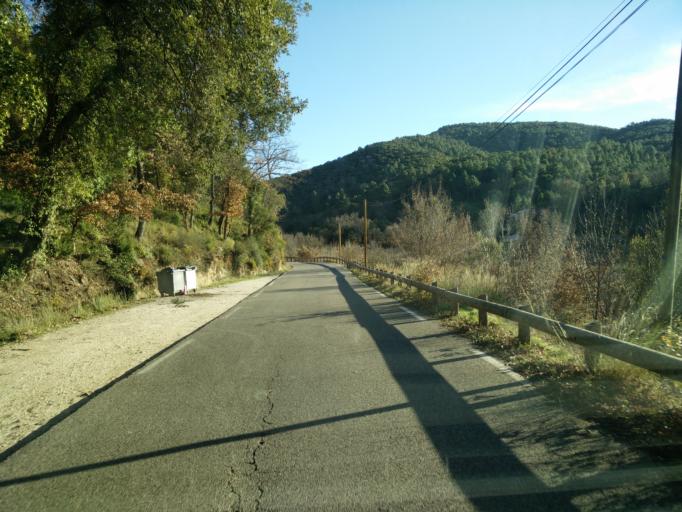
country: FR
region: Provence-Alpes-Cote d'Azur
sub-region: Departement du Var
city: Collobrieres
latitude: 43.2327
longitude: 6.2850
